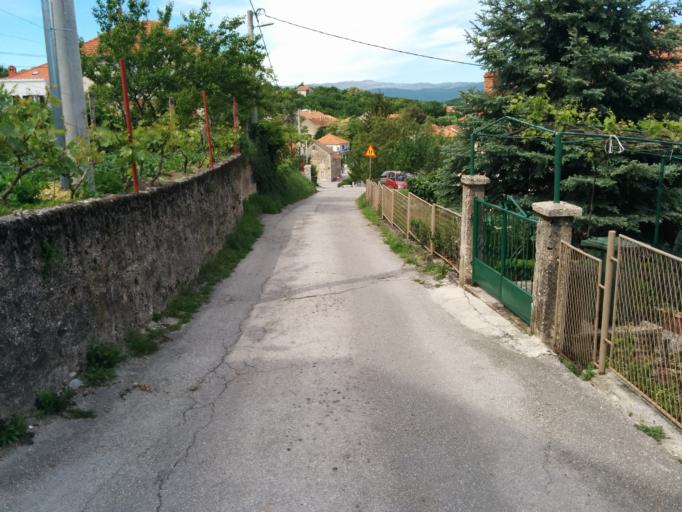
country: HR
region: Splitsko-Dalmatinska
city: Sinj
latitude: 43.7035
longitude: 16.6344
